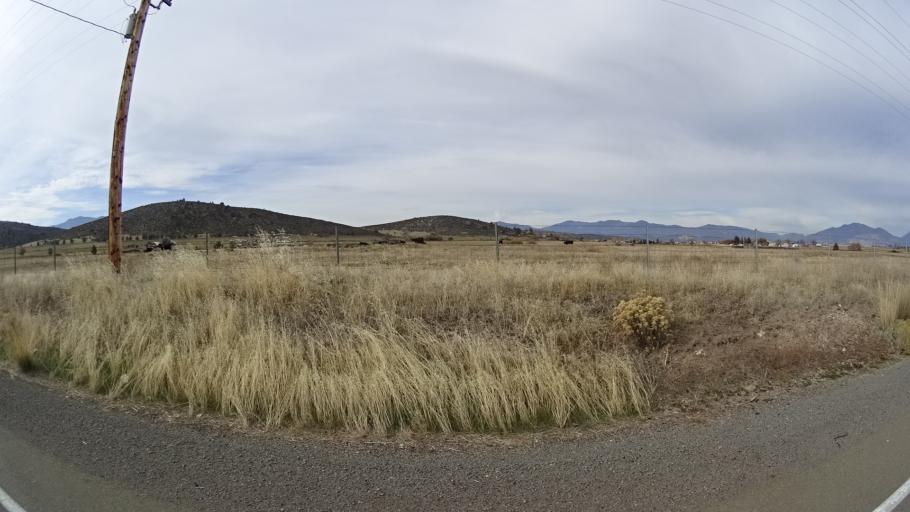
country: US
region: California
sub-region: Siskiyou County
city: Montague
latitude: 41.6943
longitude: -122.5349
